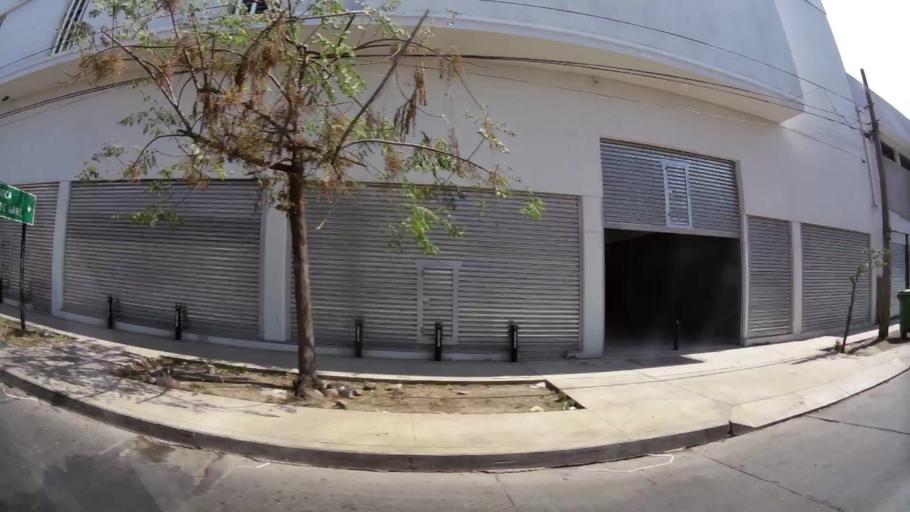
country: CL
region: Santiago Metropolitan
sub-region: Provincia de Santiago
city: Santiago
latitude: -33.4580
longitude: -70.6750
